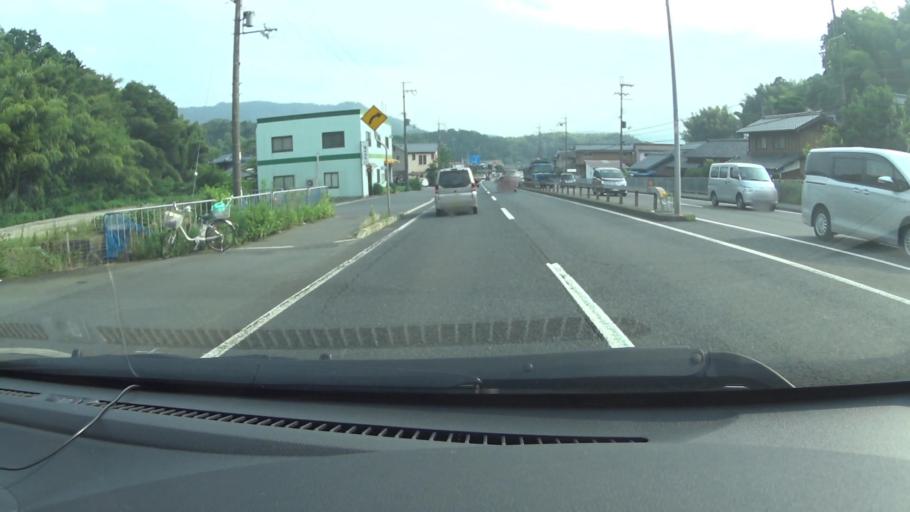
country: JP
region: Kyoto
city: Maizuru
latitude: 35.4543
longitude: 135.3492
